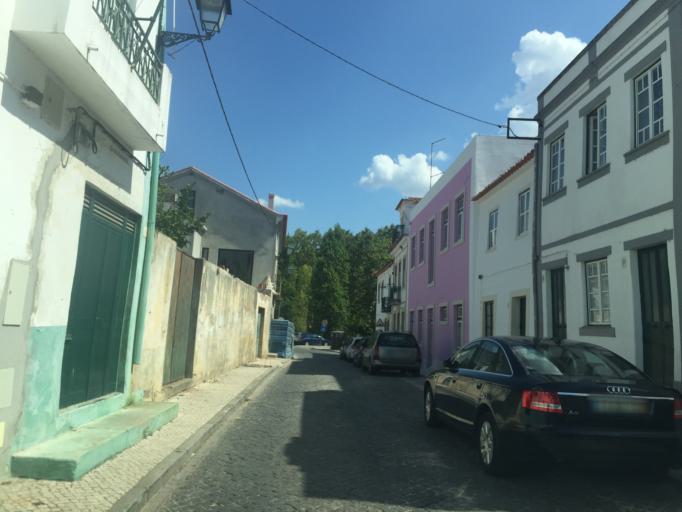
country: PT
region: Santarem
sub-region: Chamusca
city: Vila Nova da Barquinha
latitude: 39.4579
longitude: -8.4322
